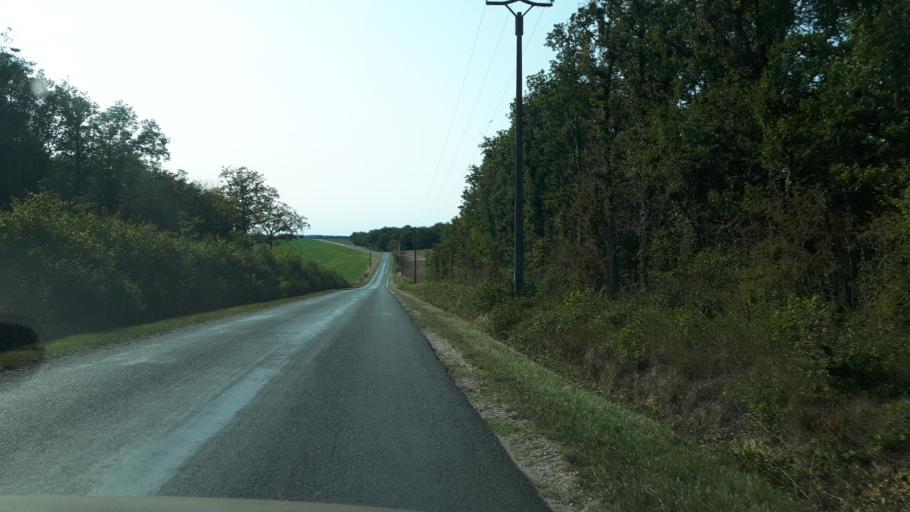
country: FR
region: Centre
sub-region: Departement du Cher
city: Rians
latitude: 47.1859
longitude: 2.6393
